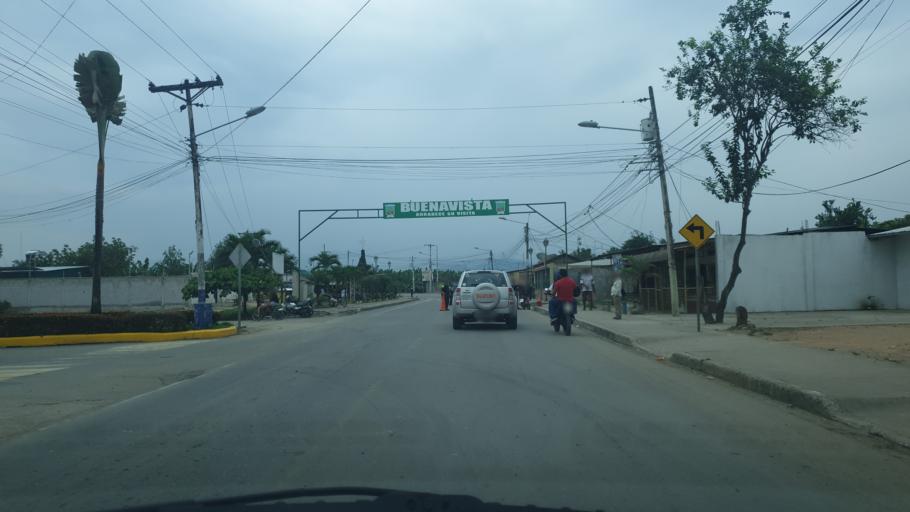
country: EC
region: El Oro
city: Pasaje
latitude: -3.3625
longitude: -79.8416
